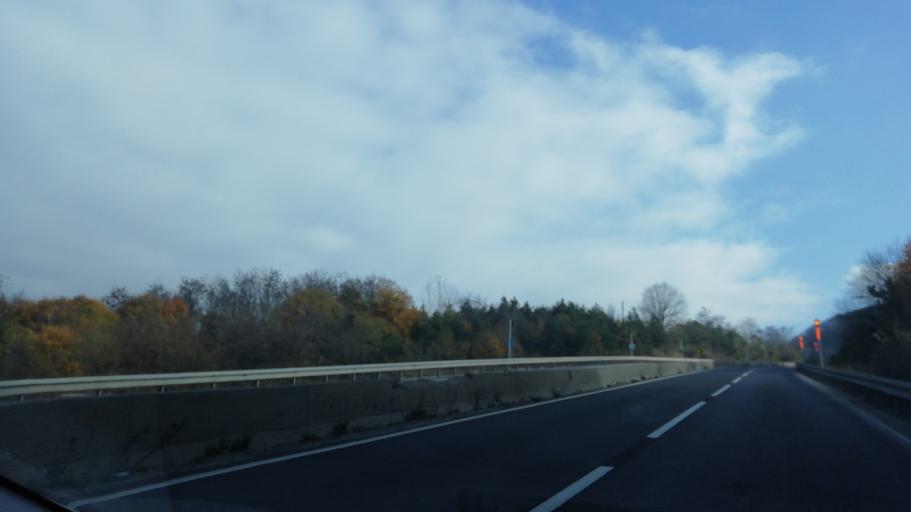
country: TR
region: Duzce
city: Kaynasli
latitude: 40.7578
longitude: 31.3575
